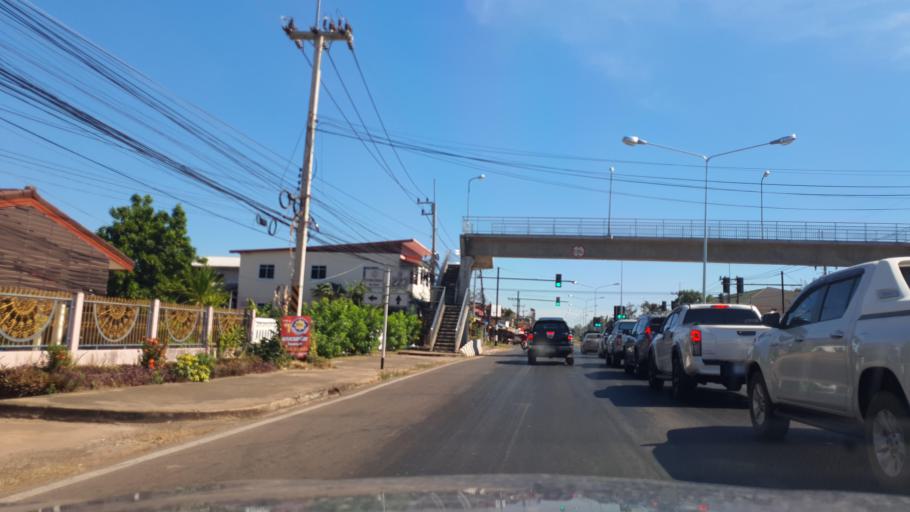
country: TH
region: Sakon Nakhon
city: Sakon Nakhon
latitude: 17.0835
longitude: 104.1900
